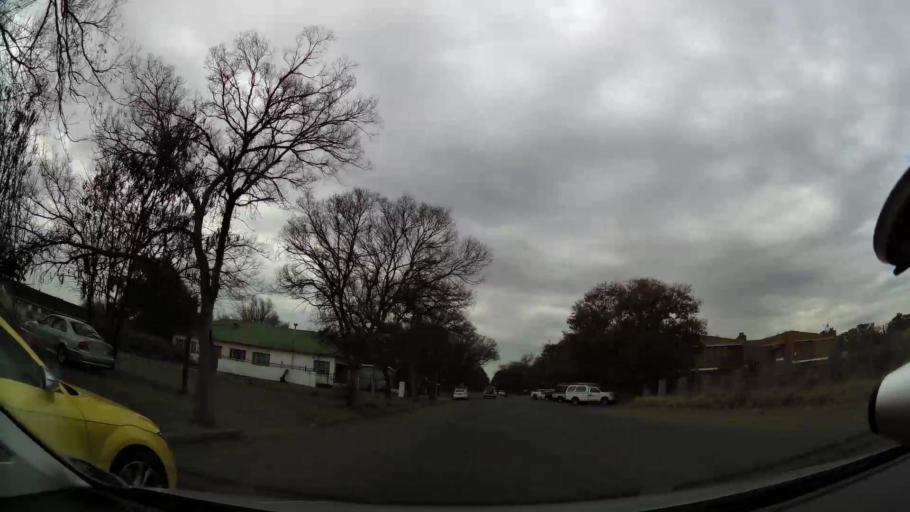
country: ZA
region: Orange Free State
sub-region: Fezile Dabi District Municipality
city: Kroonstad
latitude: -27.6625
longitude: 27.2412
